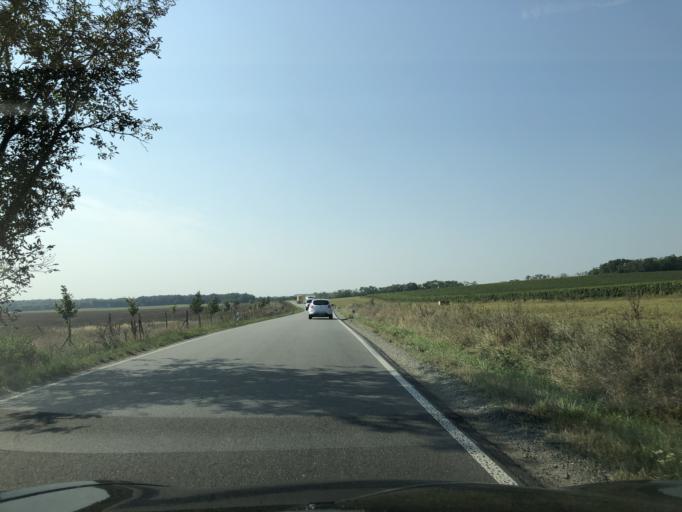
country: CZ
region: South Moravian
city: Drnholec
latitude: 48.8867
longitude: 16.5017
